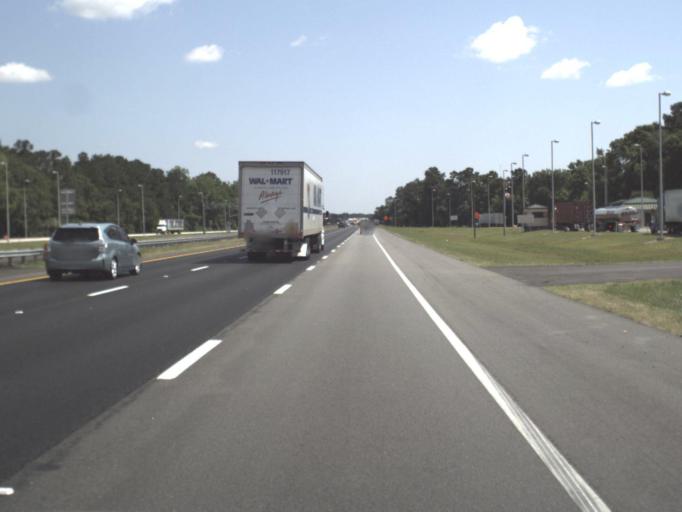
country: US
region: Georgia
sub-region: Camden County
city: Kingsland
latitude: 30.7260
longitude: -81.6636
